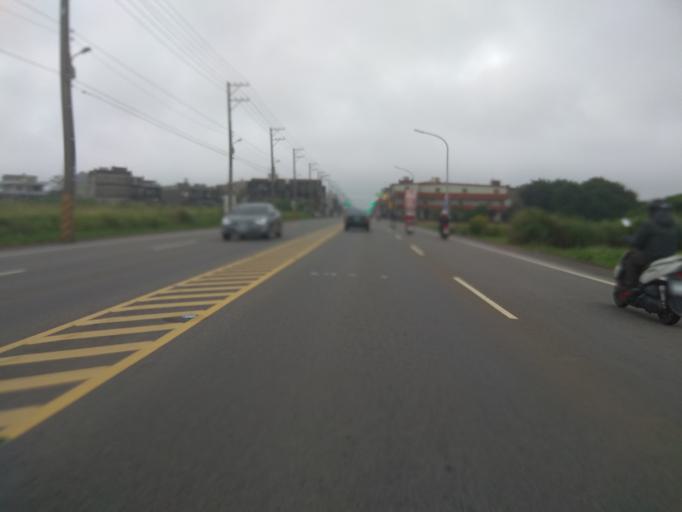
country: TW
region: Taiwan
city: Taoyuan City
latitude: 25.0243
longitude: 121.1144
